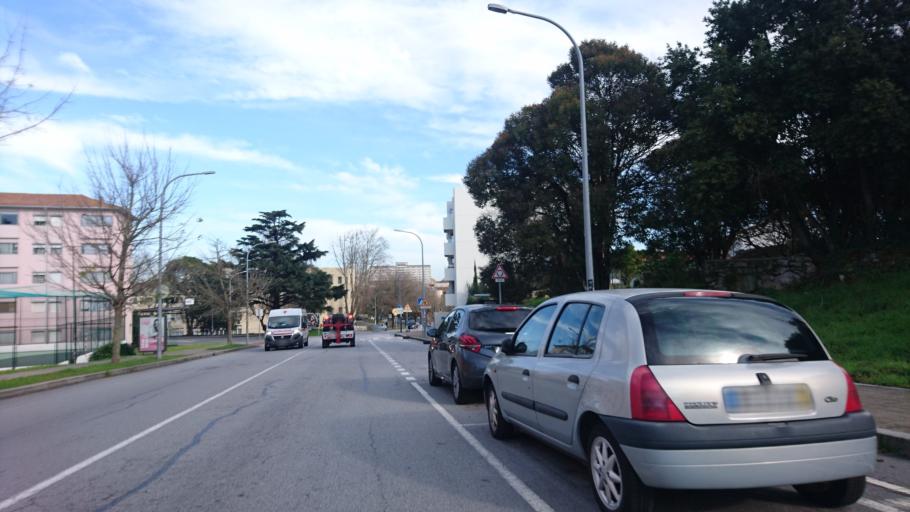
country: PT
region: Porto
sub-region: Matosinhos
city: Sao Mamede de Infesta
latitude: 41.1761
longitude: -8.6081
